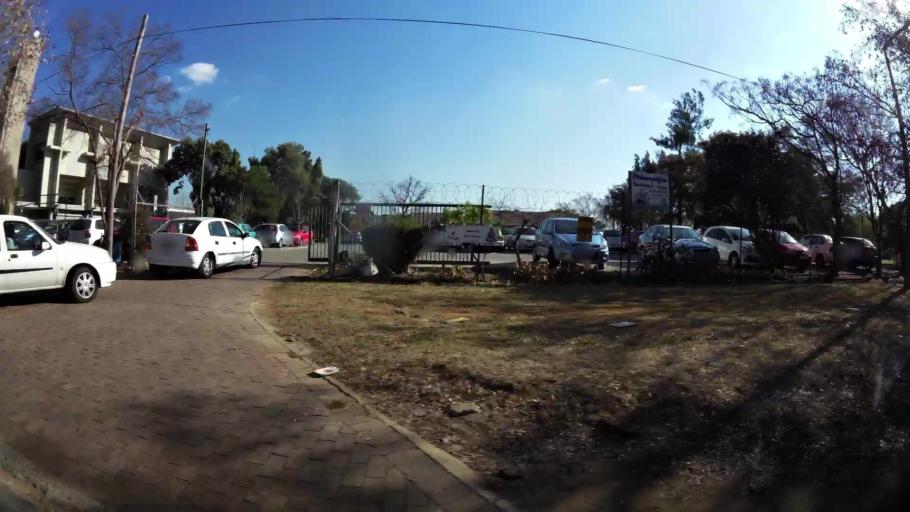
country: ZA
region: Gauteng
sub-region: Ekurhuleni Metropolitan Municipality
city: Benoni
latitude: -26.1571
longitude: 28.3279
